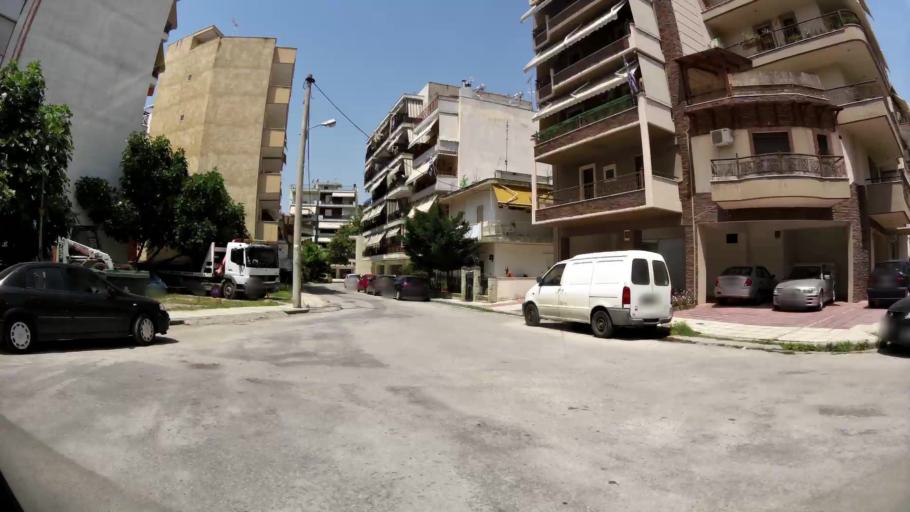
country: GR
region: Central Macedonia
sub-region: Nomos Thessalonikis
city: Menemeni
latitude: 40.6689
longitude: 22.8970
